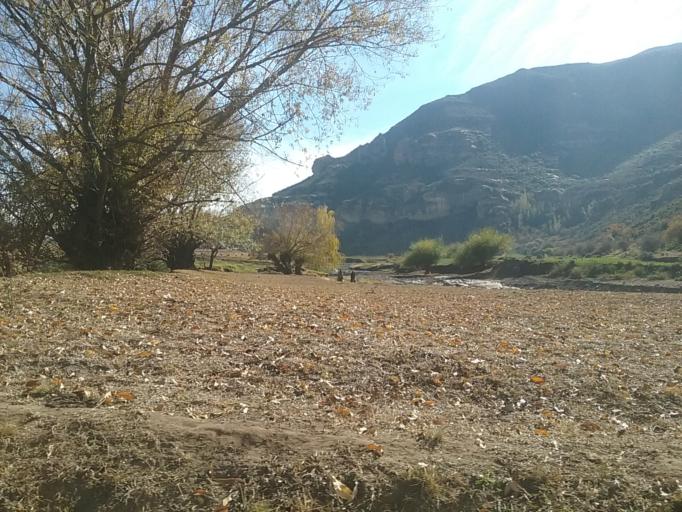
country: LS
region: Berea
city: Teyateyaneng
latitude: -29.2507
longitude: 27.9212
